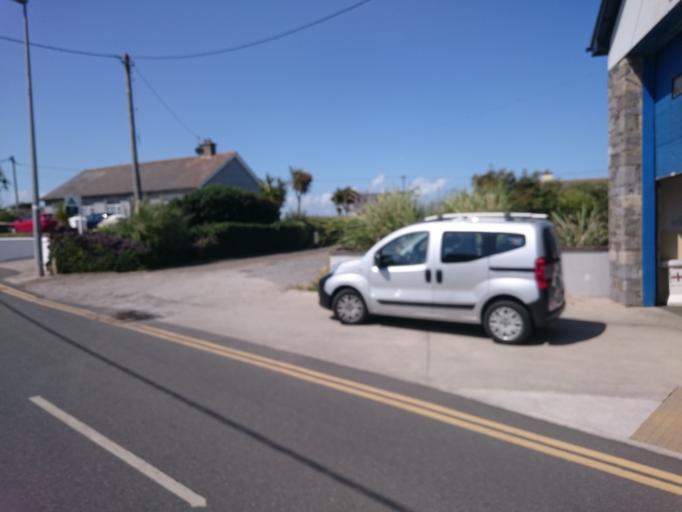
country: IE
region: Leinster
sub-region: Loch Garman
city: Loch Garman
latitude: 52.1732
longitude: -6.5899
